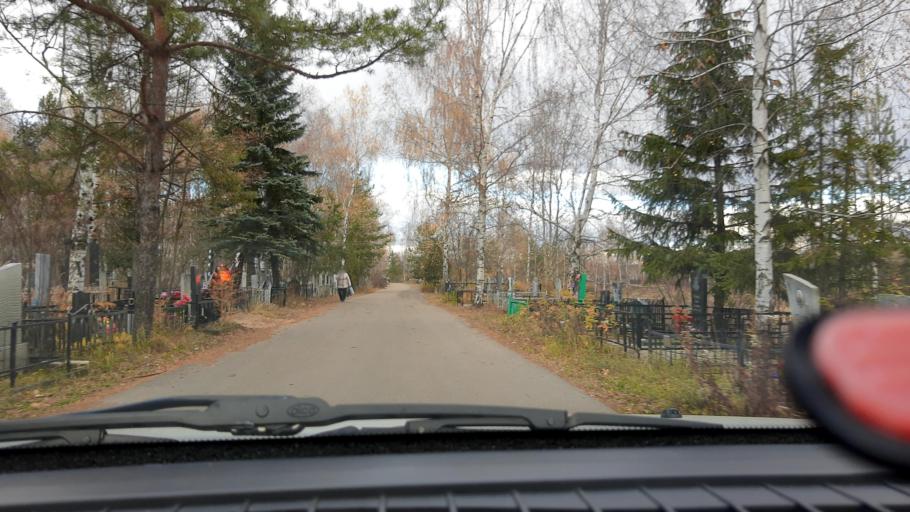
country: RU
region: Nizjnij Novgorod
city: Gorbatovka
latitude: 56.3593
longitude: 43.7878
